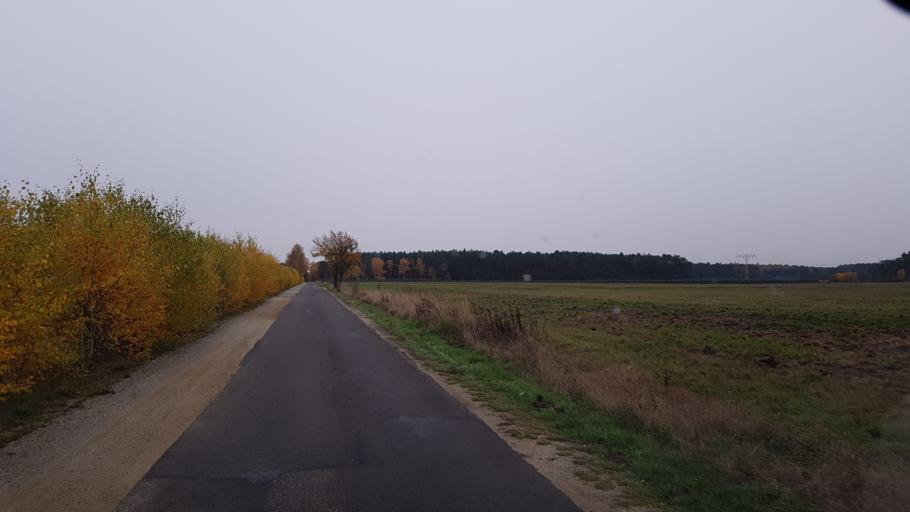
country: DE
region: Brandenburg
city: Crinitz
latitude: 51.7223
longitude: 13.7729
